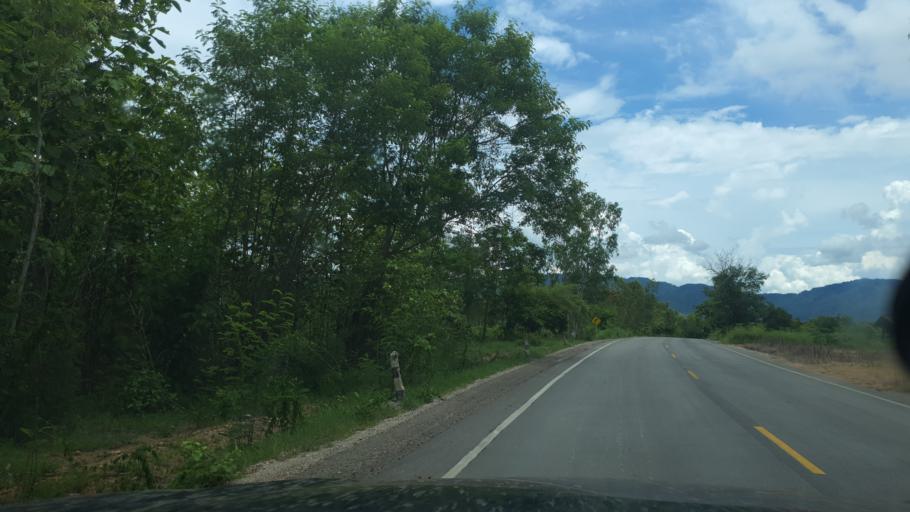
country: TH
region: Lampang
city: Sop Prap
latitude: 17.9232
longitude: 99.3831
